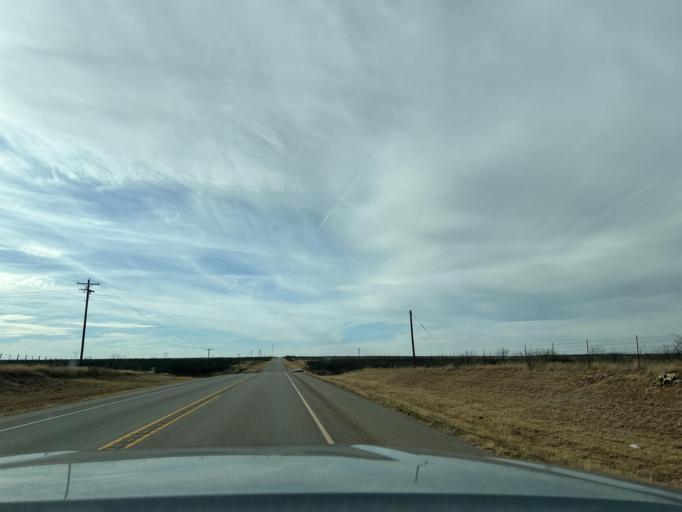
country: US
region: Texas
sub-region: Jones County
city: Anson
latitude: 32.7506
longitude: -99.6994
